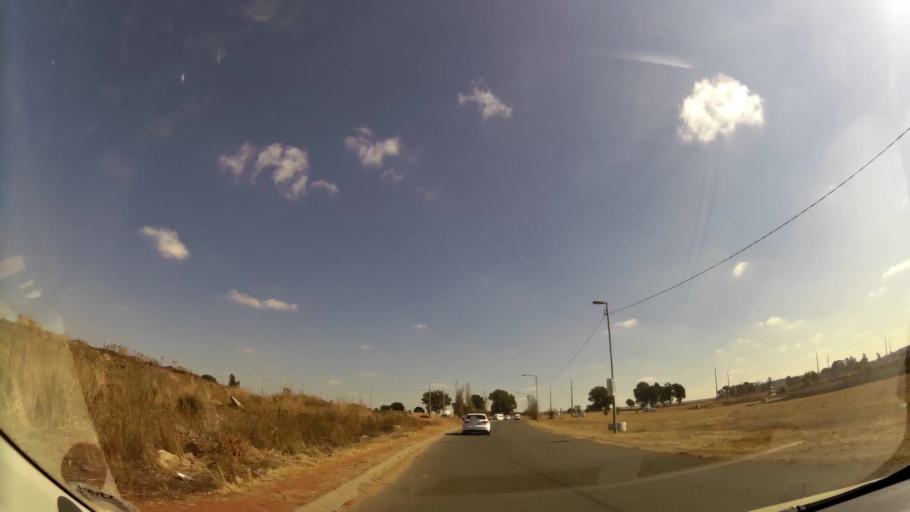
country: ZA
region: Gauteng
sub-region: West Rand District Municipality
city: Randfontein
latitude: -26.1561
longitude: 27.7640
